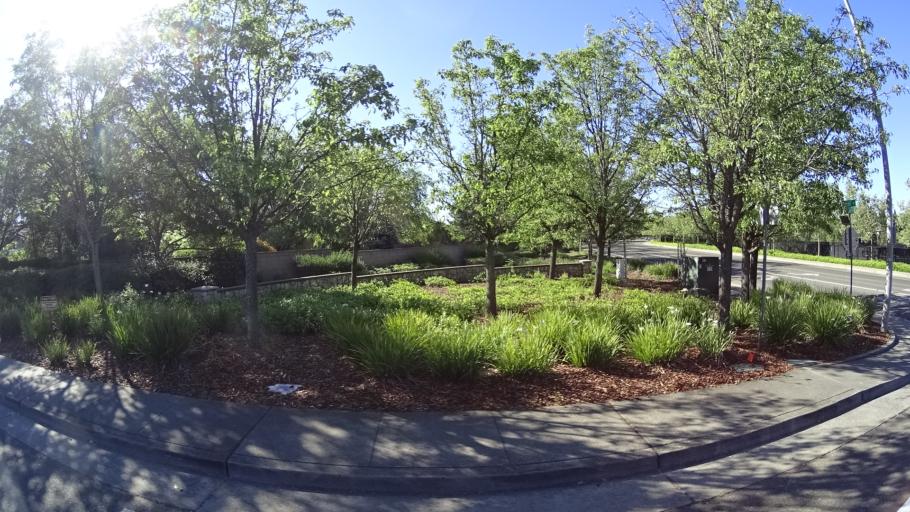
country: US
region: California
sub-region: Placer County
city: Rocklin
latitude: 38.8206
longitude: -121.2378
